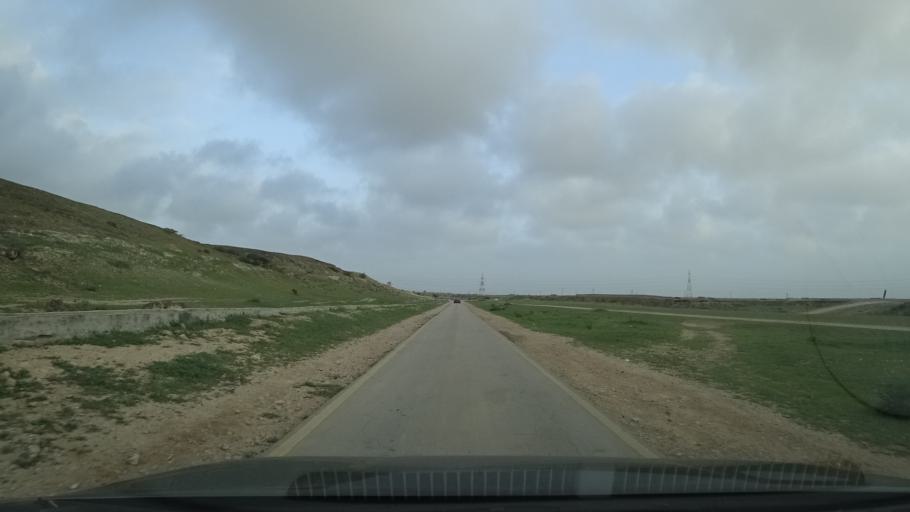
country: OM
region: Zufar
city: Salalah
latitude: 17.1109
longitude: 54.2278
